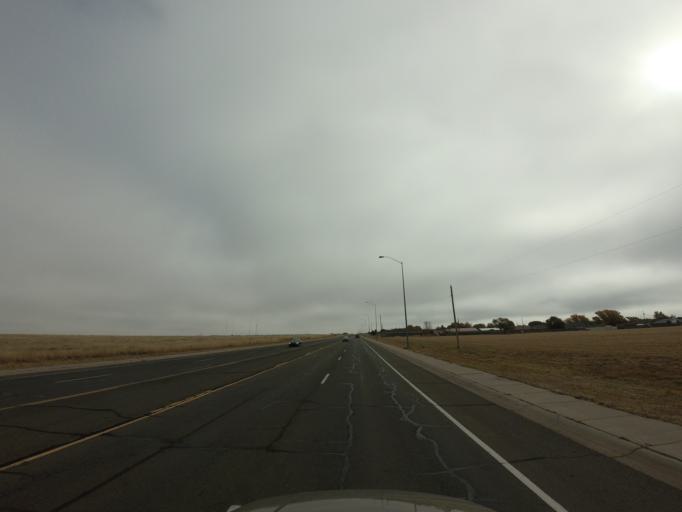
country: US
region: New Mexico
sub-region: Curry County
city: Clovis
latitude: 34.4340
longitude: -103.2304
